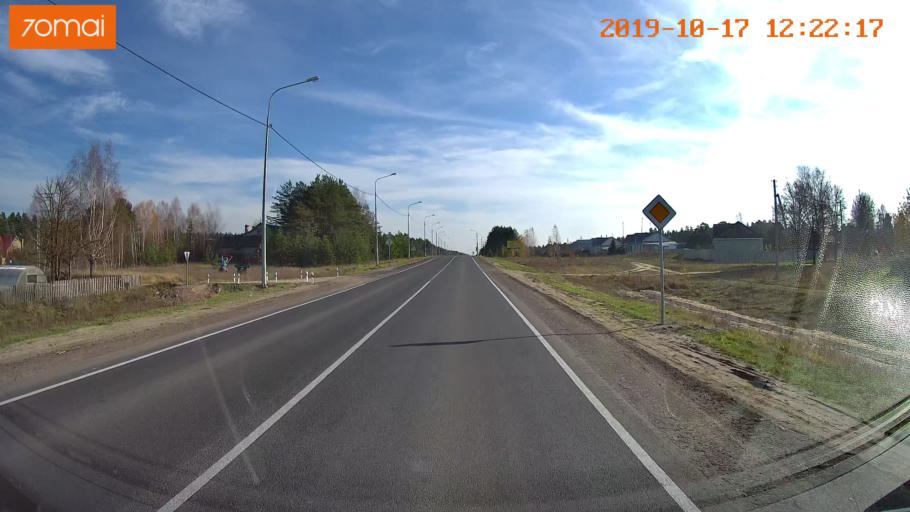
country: RU
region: Rjazan
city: Gus'-Zheleznyy
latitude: 55.0529
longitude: 41.1692
